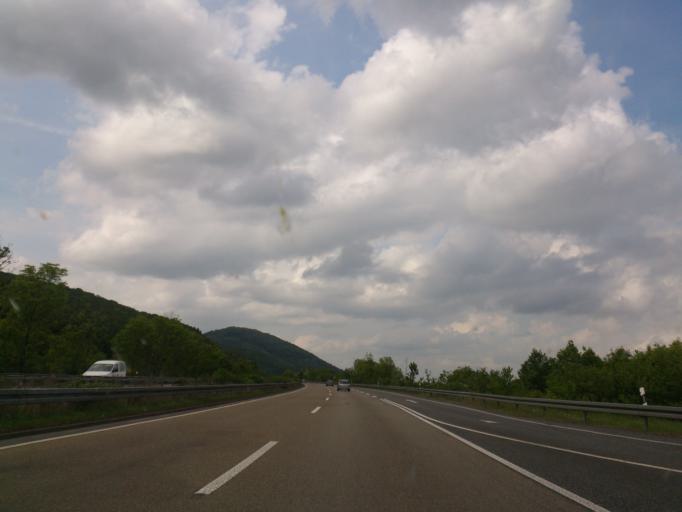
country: DE
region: Hesse
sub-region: Regierungsbezirk Kassel
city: Zierenberg
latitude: 51.3431
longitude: 9.2831
